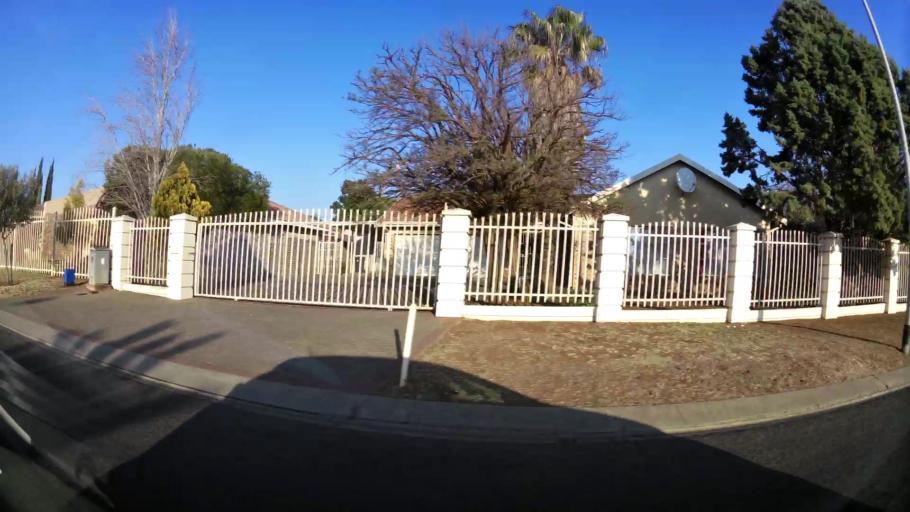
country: ZA
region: Orange Free State
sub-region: Mangaung Metropolitan Municipality
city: Bloemfontein
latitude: -29.1520
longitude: 26.1651
